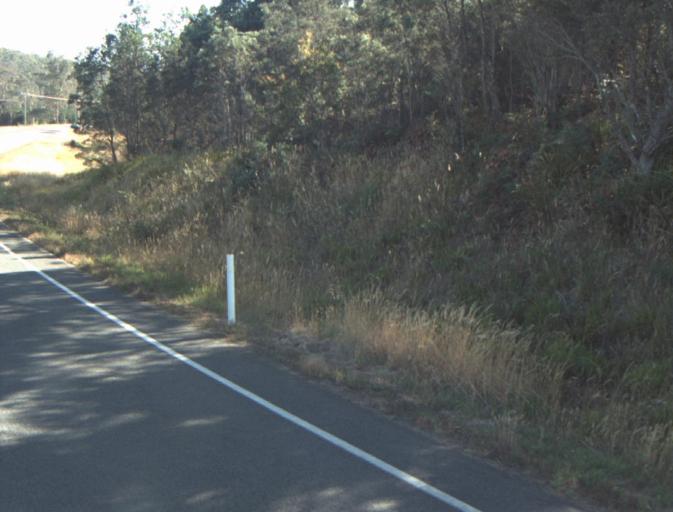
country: AU
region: Tasmania
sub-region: Launceston
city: Newstead
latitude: -41.4081
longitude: 147.2806
